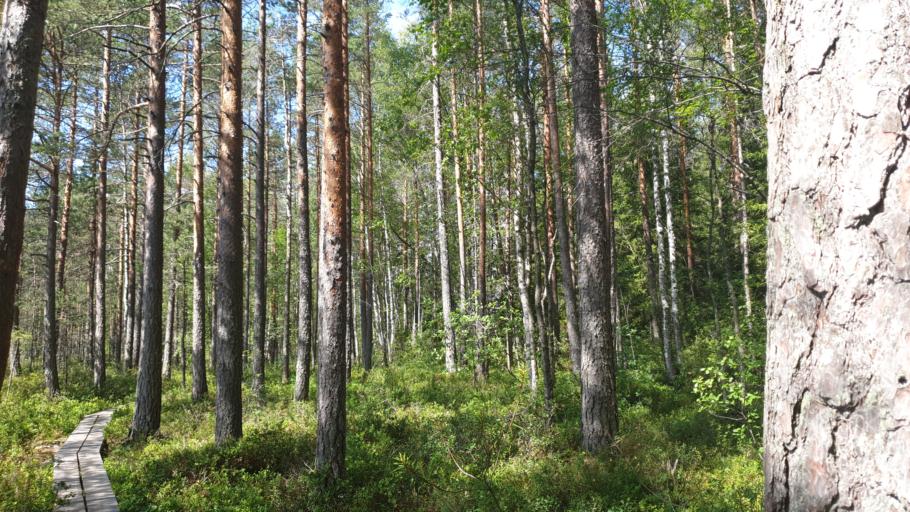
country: FI
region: Uusimaa
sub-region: Helsinki
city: Kirkkonummi
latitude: 60.3118
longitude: 24.4883
